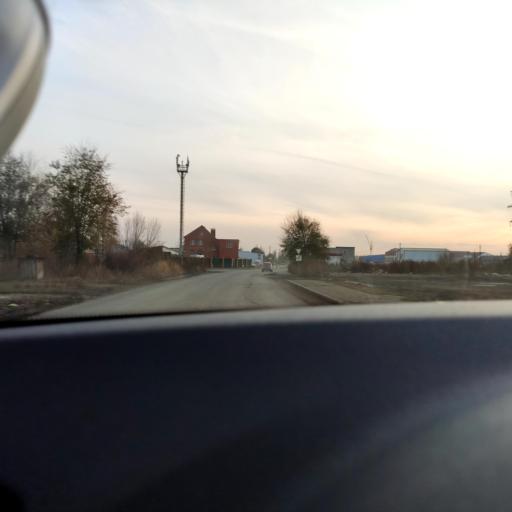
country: RU
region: Samara
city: Petra-Dubrava
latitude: 53.2559
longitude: 50.3120
